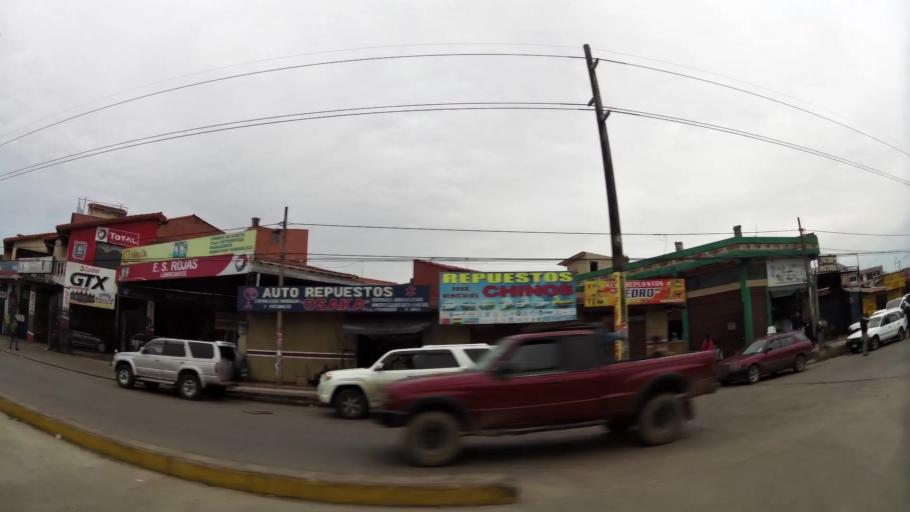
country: BO
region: Santa Cruz
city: Santa Cruz de la Sierra
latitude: -17.8094
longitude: -63.1921
